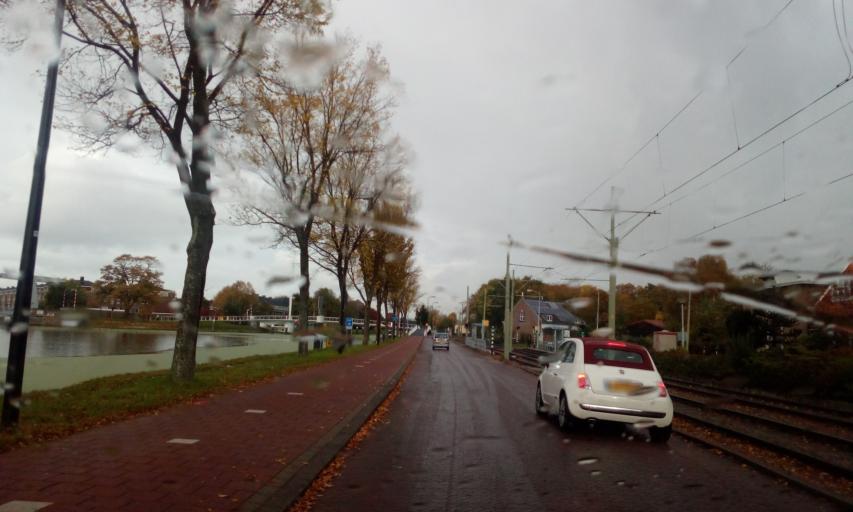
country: NL
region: South Holland
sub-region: Gemeente Rijswijk
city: Rijswijk
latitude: 52.0441
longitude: 4.3443
